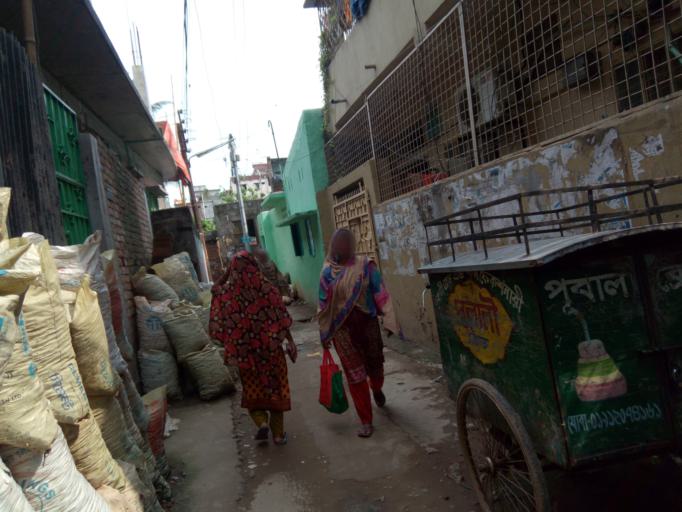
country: BD
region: Dhaka
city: Azimpur
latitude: 23.7388
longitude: 90.3646
